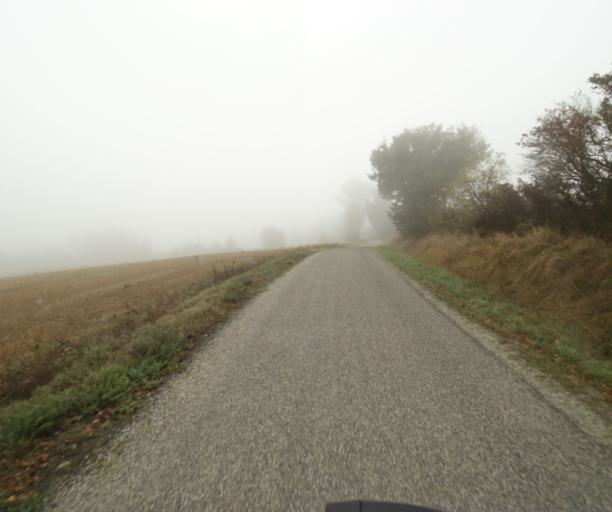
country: FR
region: Midi-Pyrenees
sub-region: Departement de la Haute-Garonne
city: Villemur-sur-Tarn
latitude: 43.8947
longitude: 1.4825
